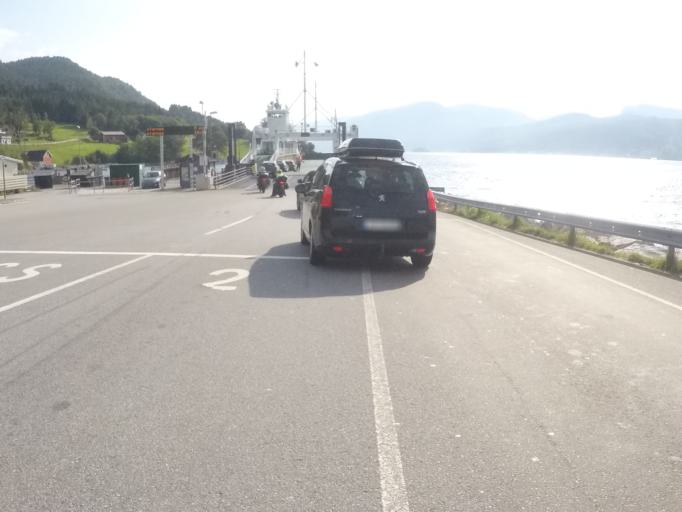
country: NO
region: More og Romsdal
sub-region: Molde
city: Hjelset
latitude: 62.6848
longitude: 7.4636
